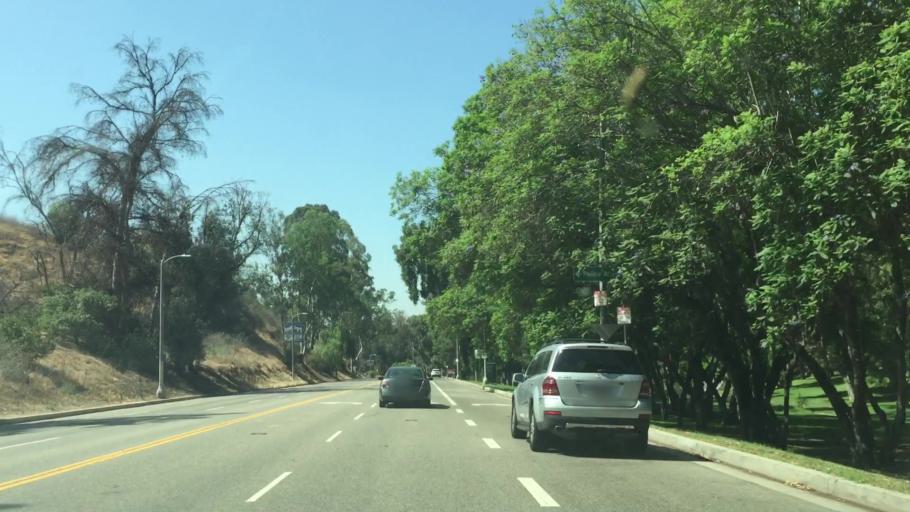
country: US
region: California
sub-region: Los Angeles County
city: Echo Park
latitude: 34.0832
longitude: -118.2461
